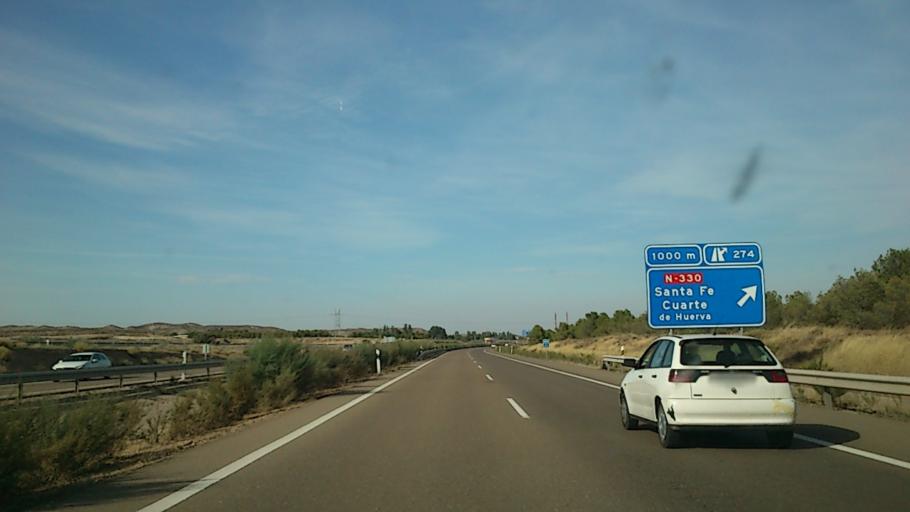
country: ES
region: Aragon
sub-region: Provincia de Zaragoza
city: Cuarte de Huerva
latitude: 41.5826
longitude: -0.9562
